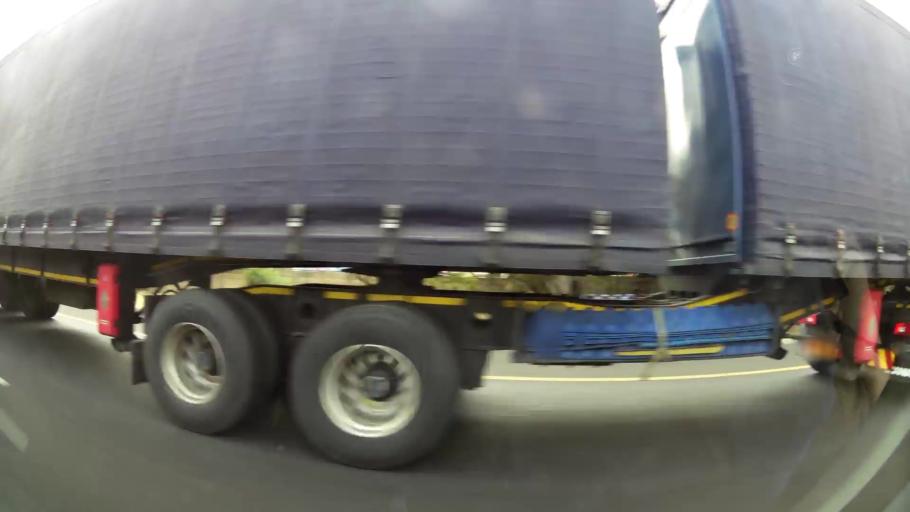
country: ZA
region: Orange Free State
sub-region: Mangaung Metropolitan Municipality
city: Bloemfontein
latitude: -29.1518
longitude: 26.1742
